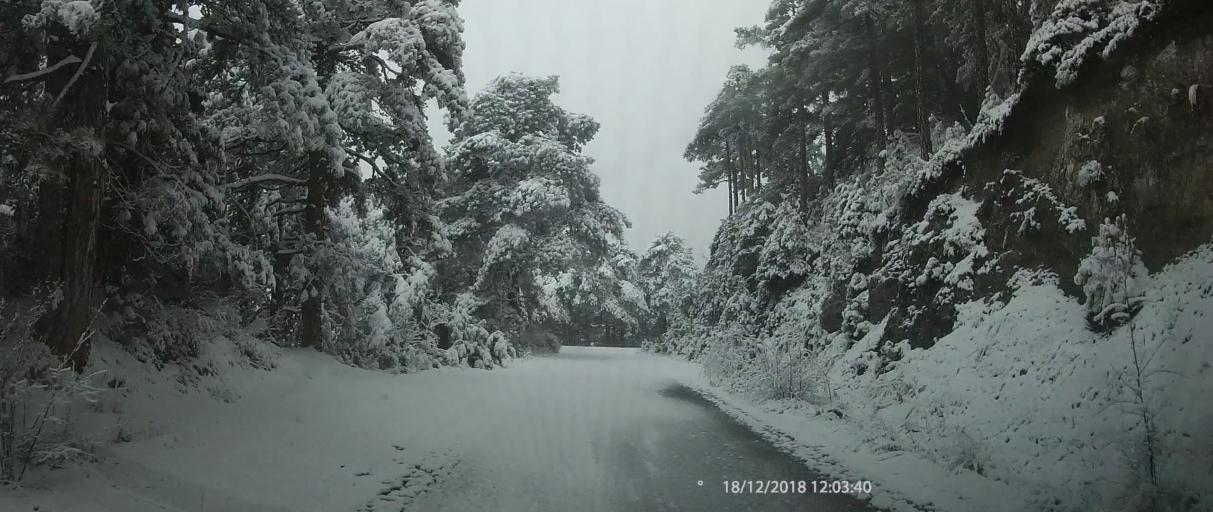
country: GR
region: Central Macedonia
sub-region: Nomos Pierias
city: Litochoro
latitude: 40.1068
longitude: 22.4638
